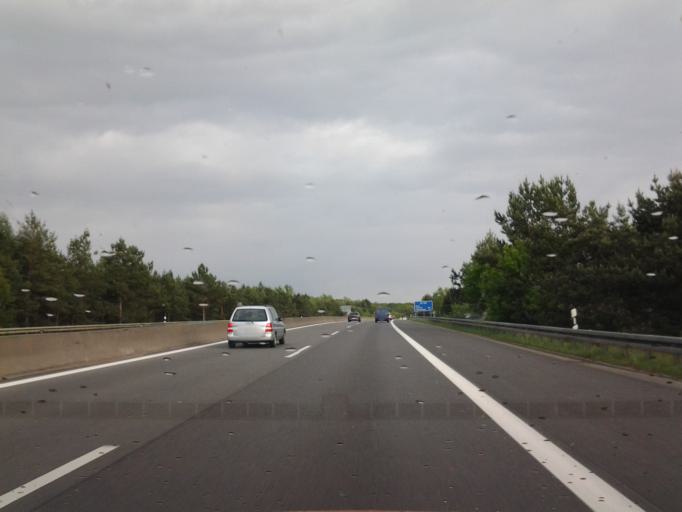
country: DE
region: Brandenburg
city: Hennigsdorf
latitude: 52.6754
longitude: 13.2304
